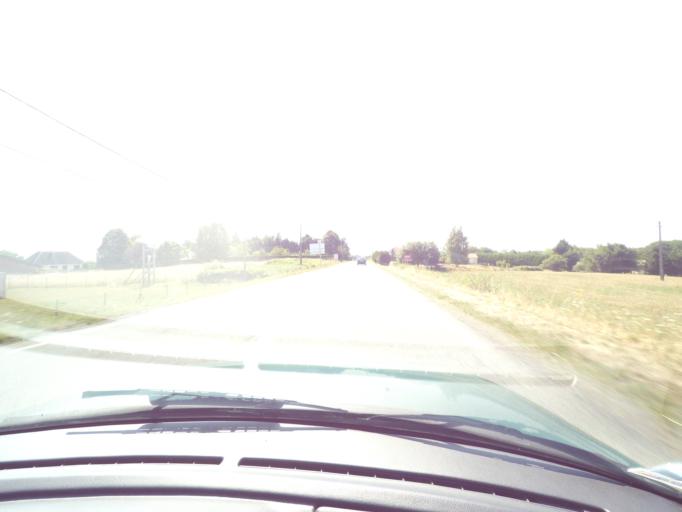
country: FR
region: Limousin
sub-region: Departement de la Haute-Vienne
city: Chaptelat
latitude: 45.9087
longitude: 1.2206
